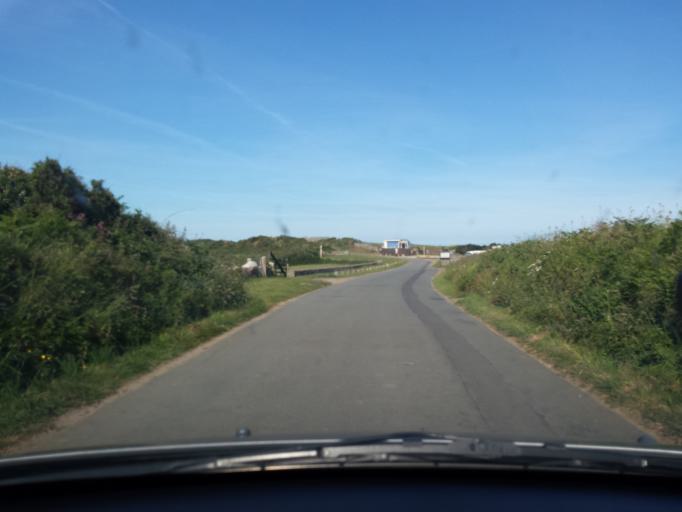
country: FR
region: Lower Normandy
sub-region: Departement de la Manche
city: Beaumont-Hague
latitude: 49.6773
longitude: -1.9372
